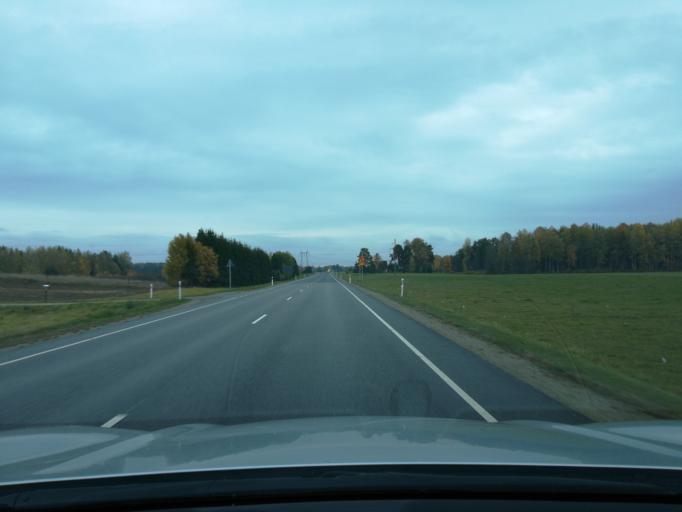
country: EE
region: Ida-Virumaa
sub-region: Johvi vald
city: Johvi
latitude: 59.0803
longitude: 27.3158
